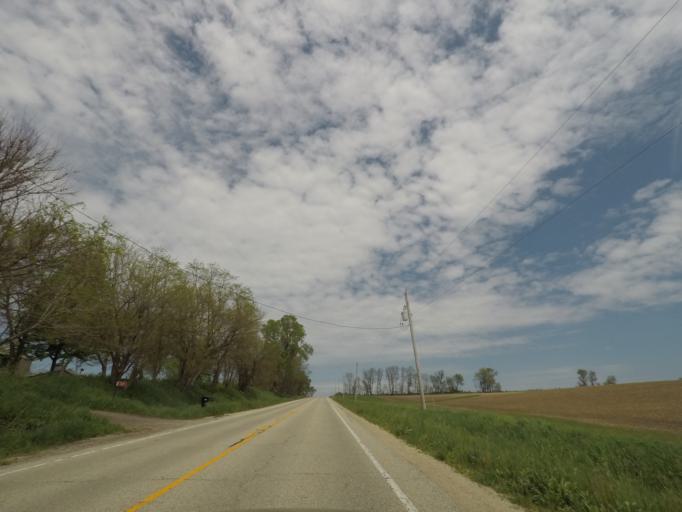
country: US
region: Wisconsin
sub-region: Rock County
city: Evansville
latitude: 42.7061
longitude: -89.2888
